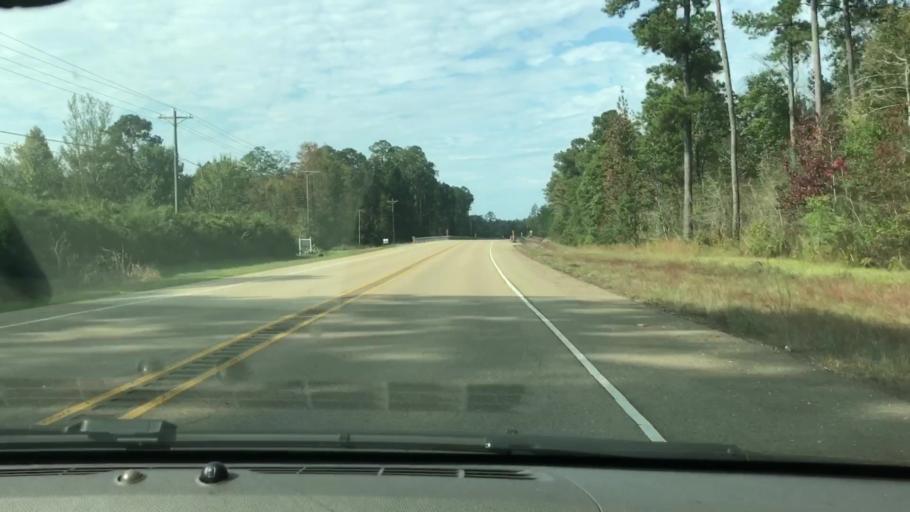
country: US
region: Louisiana
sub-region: Saint Tammany Parish
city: Abita Springs
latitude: 30.5057
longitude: -89.9742
